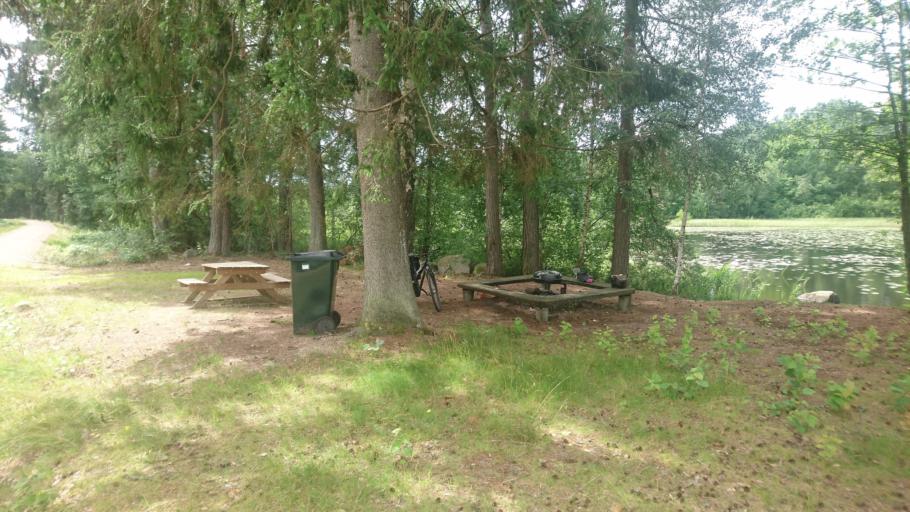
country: SE
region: Kronoberg
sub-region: Vaxjo Kommun
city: Vaexjoe
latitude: 56.8294
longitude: 14.8730
